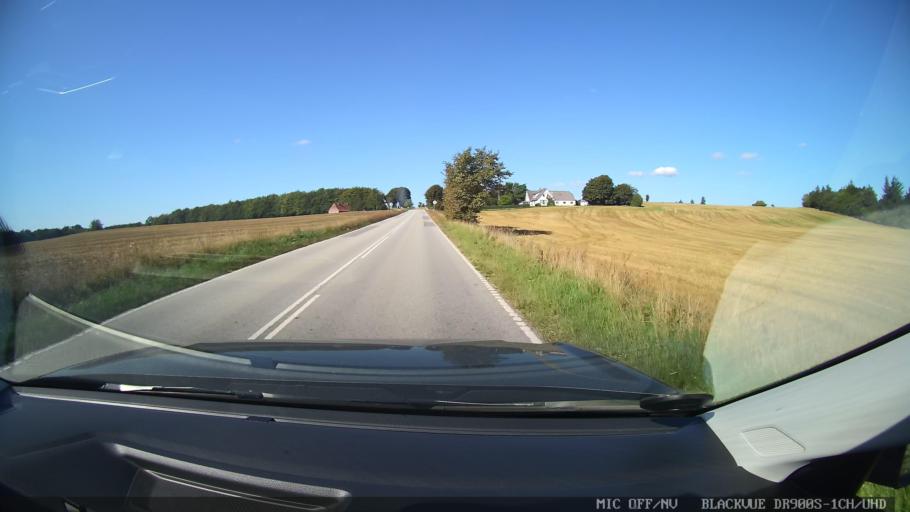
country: DK
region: North Denmark
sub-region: Mariagerfjord Kommune
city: Mariager
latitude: 56.6110
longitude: 9.9916
